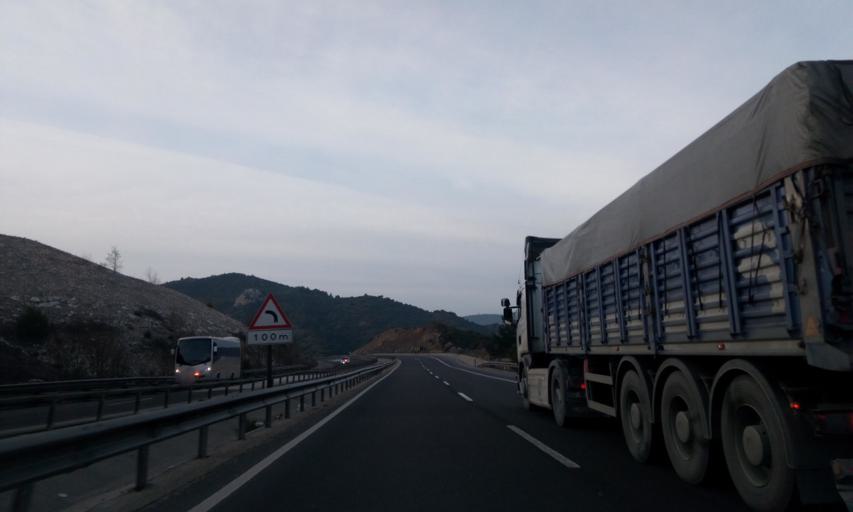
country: TR
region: Bilecik
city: Bilecik
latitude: 40.1609
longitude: 30.0202
